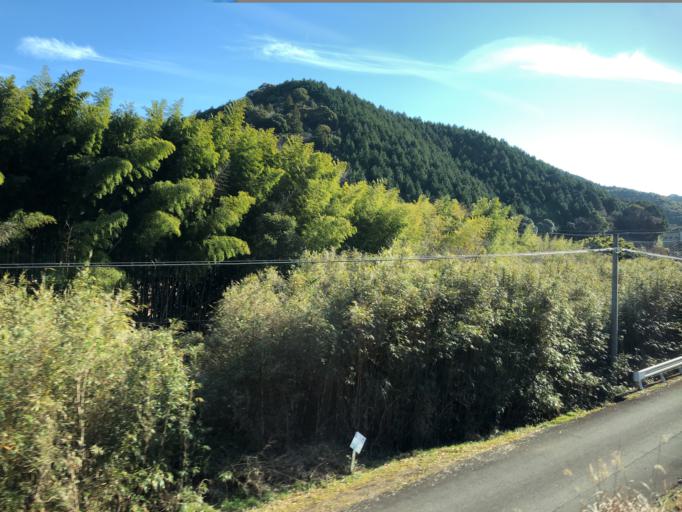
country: JP
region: Kochi
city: Nakamura
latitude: 33.1216
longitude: 133.1184
